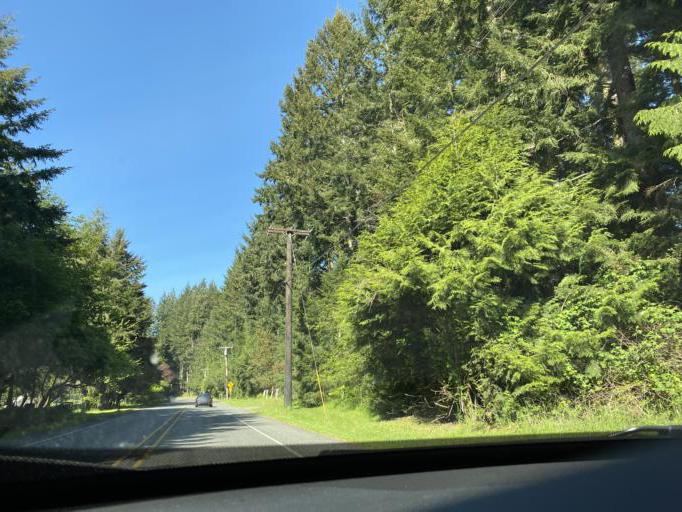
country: US
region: Washington
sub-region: Island County
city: Langley
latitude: 48.0284
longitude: -122.4487
